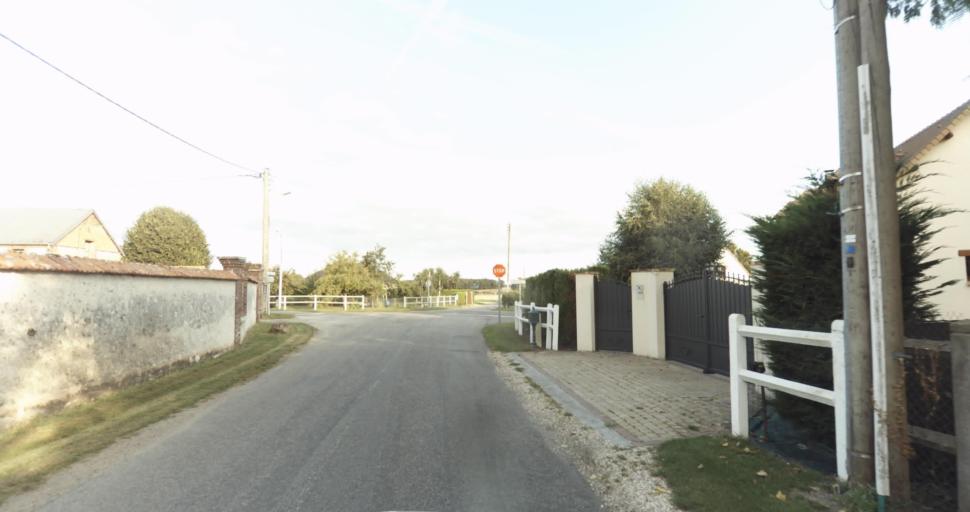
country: FR
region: Haute-Normandie
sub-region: Departement de l'Eure
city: Marcilly-sur-Eure
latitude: 48.8374
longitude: 1.2816
